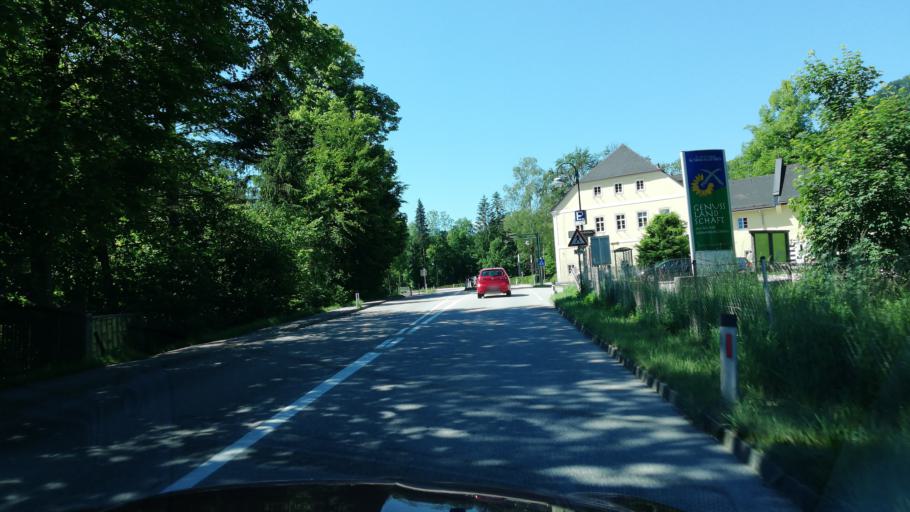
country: AT
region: Upper Austria
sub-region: Politischer Bezirk Kirchdorf an der Krems
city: Gruenburg
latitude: 47.9087
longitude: 14.2358
